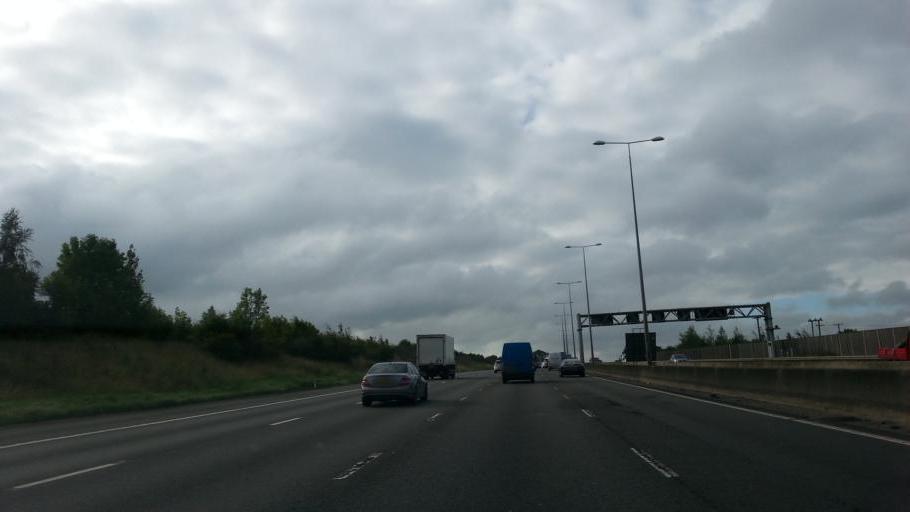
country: GB
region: England
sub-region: Hertfordshire
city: Redbourn
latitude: 51.7842
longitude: -0.4108
